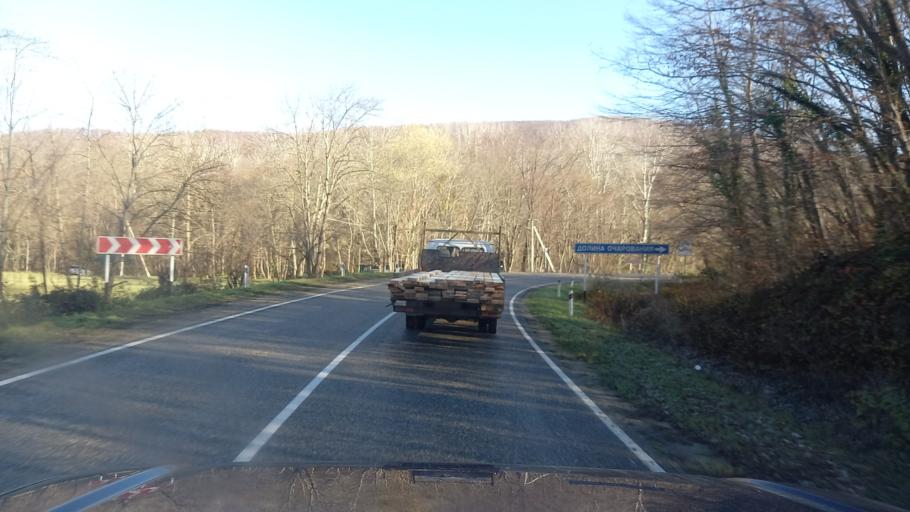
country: RU
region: Krasnodarskiy
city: Goryachiy Klyuch
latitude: 44.6066
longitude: 39.0793
